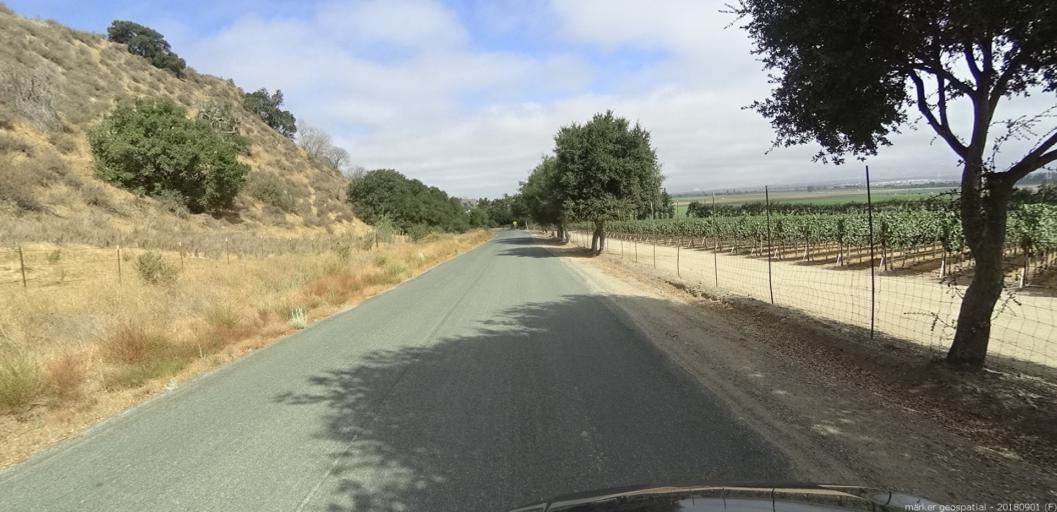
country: US
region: California
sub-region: Monterey County
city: Soledad
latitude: 36.4096
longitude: -121.3895
